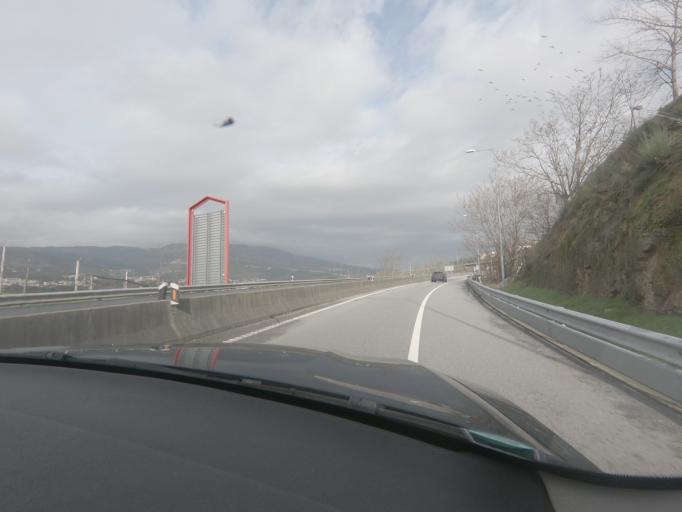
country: PT
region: Vila Real
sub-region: Vila Real
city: Vila Real
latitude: 41.2974
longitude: -7.7556
